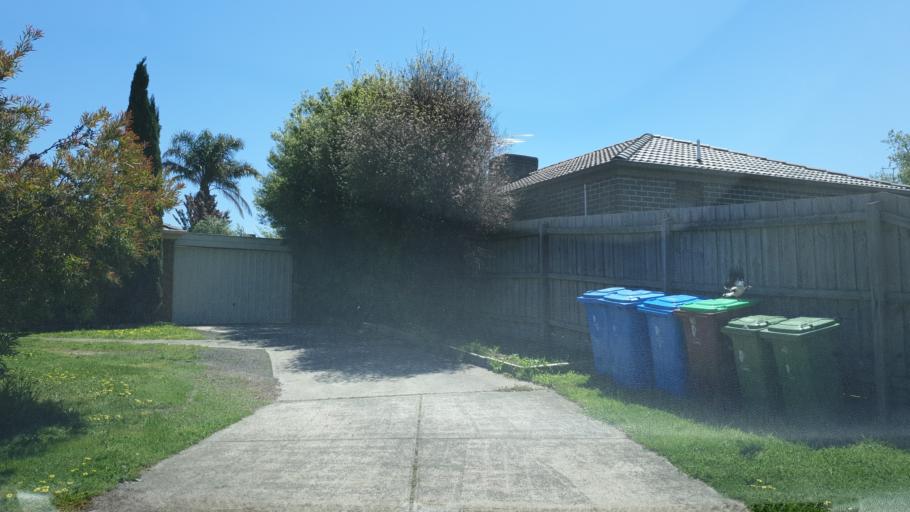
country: AU
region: Victoria
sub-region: Casey
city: Cranbourne North
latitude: -38.0828
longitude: 145.2854
